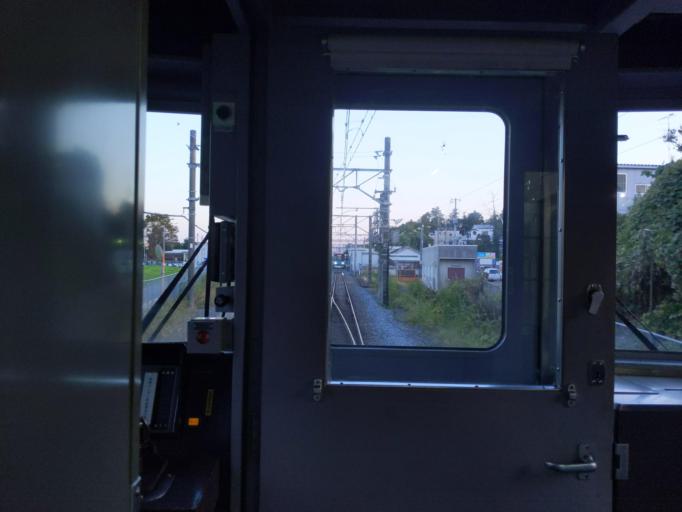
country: JP
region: Chiba
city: Noda
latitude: 35.9602
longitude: 139.8592
